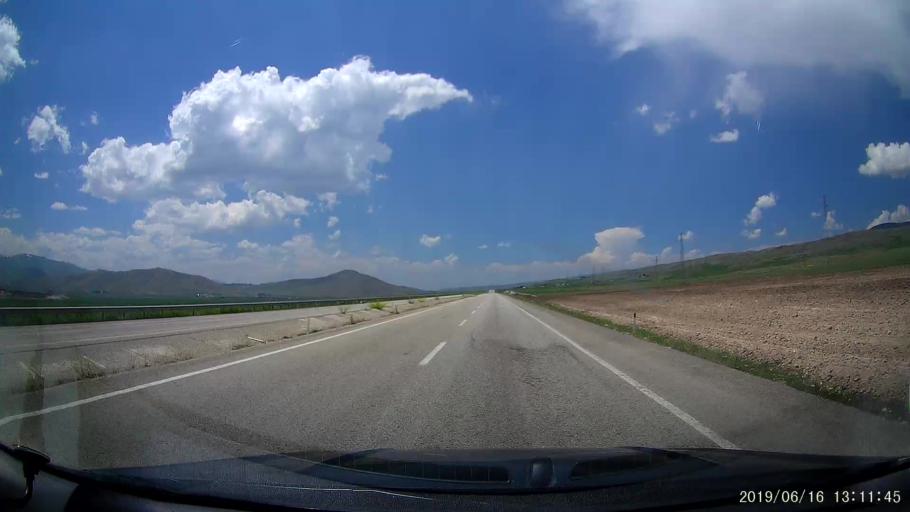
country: TR
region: Agri
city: Diyadin
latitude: 39.5934
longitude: 43.5989
